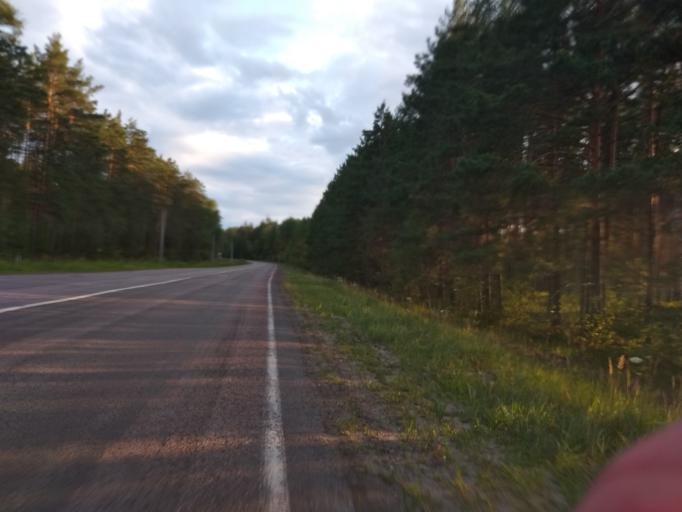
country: RU
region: Moskovskaya
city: Misheronskiy
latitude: 55.6263
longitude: 39.7375
